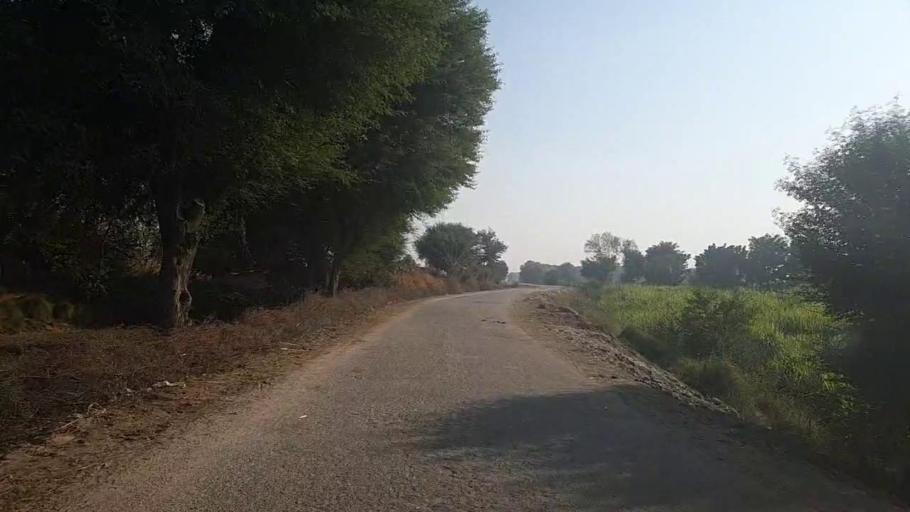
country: PK
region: Sindh
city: Kot Diji
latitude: 27.2654
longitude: 68.6748
